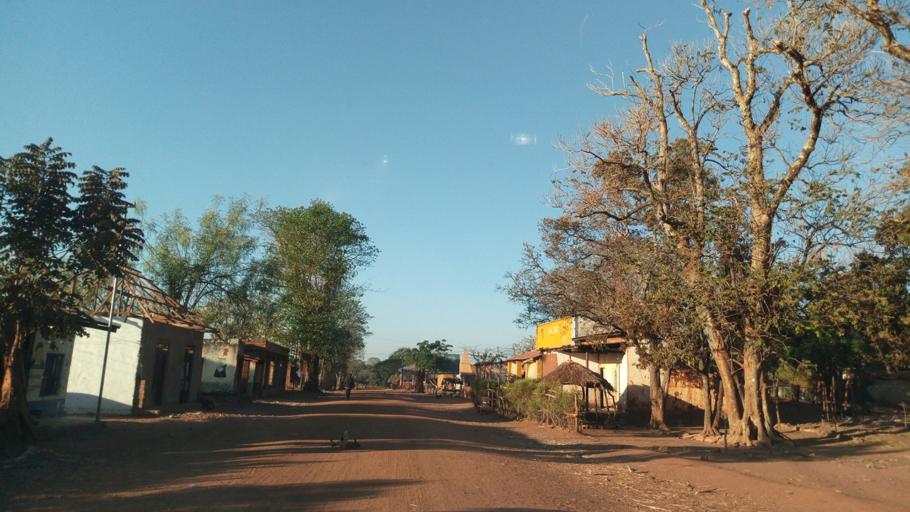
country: ZM
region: Luapula
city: Mwense
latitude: -10.3699
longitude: 28.6154
